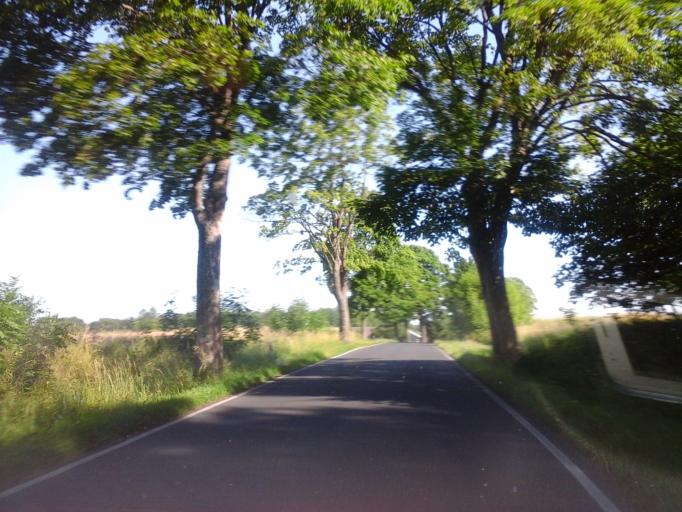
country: PL
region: West Pomeranian Voivodeship
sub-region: Powiat drawski
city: Zlocieniec
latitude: 53.6179
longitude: 15.9226
